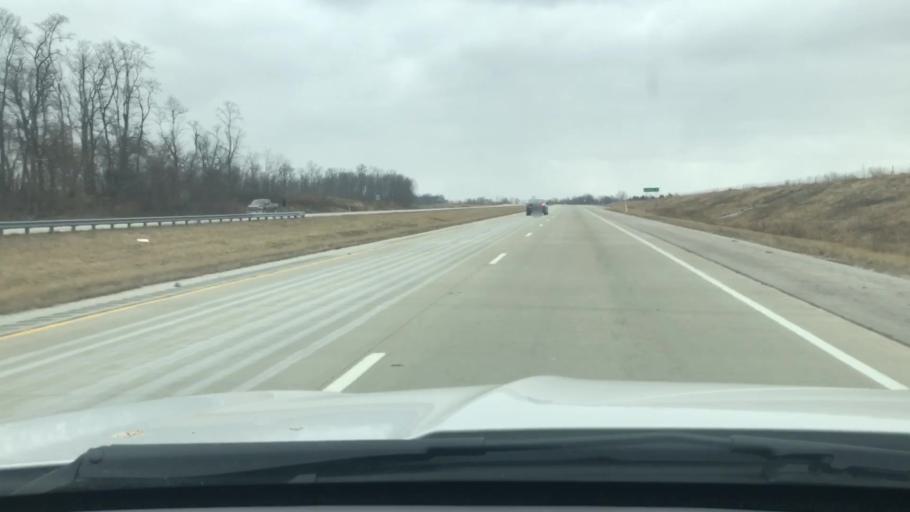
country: US
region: Indiana
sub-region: Carroll County
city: Delphi
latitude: 40.5143
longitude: -86.7220
